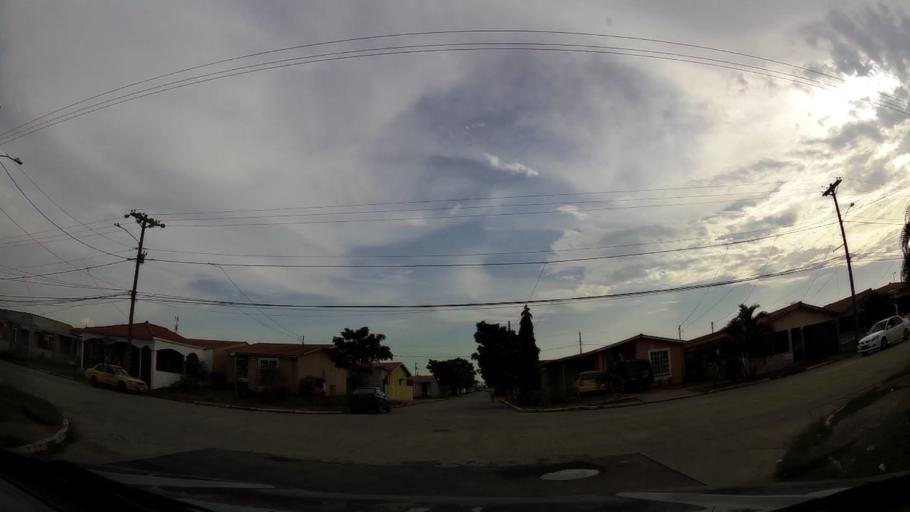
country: PA
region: Panama
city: Tocumen
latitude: 9.0740
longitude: -79.3616
